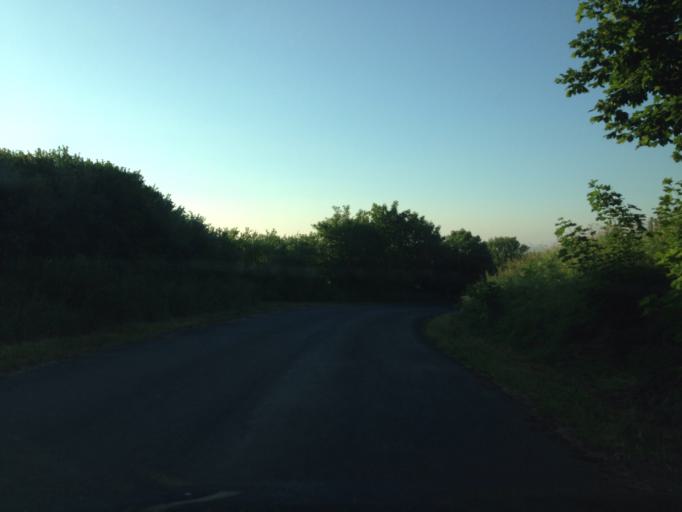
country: PL
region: Pomeranian Voivodeship
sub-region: Powiat tczewski
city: Gniew
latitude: 53.7797
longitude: 18.8298
